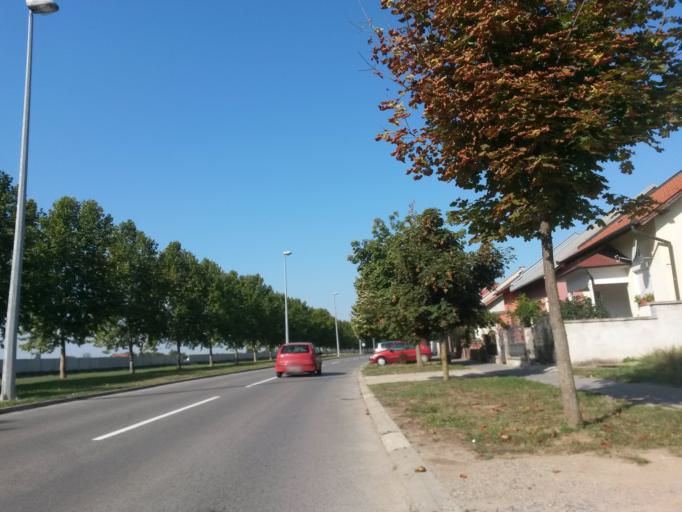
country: HR
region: Osjecko-Baranjska
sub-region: Grad Osijek
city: Osijek
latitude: 45.5413
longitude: 18.7070
